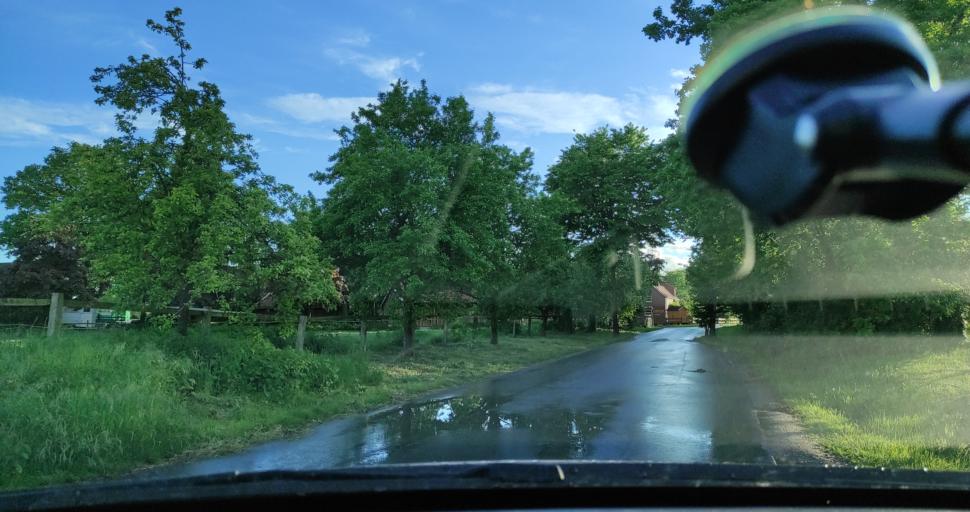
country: DE
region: North Rhine-Westphalia
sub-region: Regierungsbezirk Munster
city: Greven
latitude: 52.1024
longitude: 7.5816
